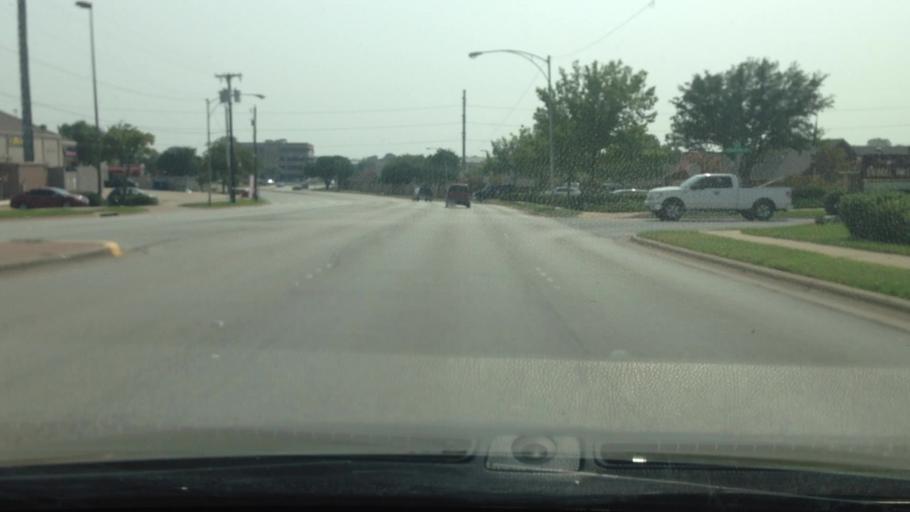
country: US
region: Texas
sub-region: Tarrant County
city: Colleyville
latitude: 32.8672
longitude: -97.1739
